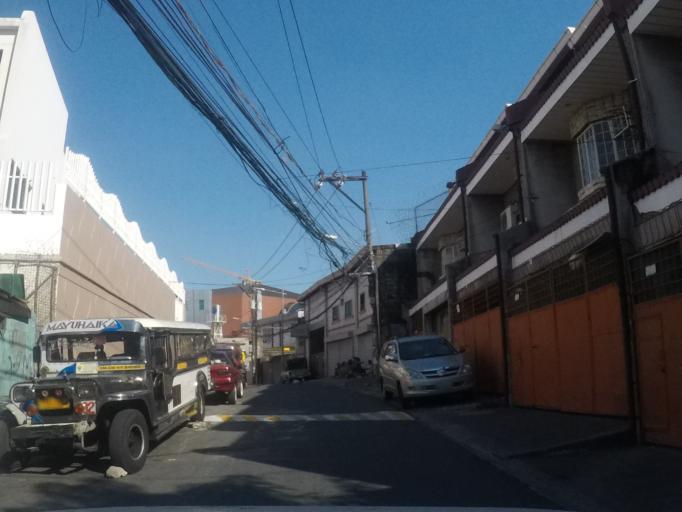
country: PH
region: Metro Manila
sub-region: San Juan
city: San Juan
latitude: 14.6066
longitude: 121.0316
